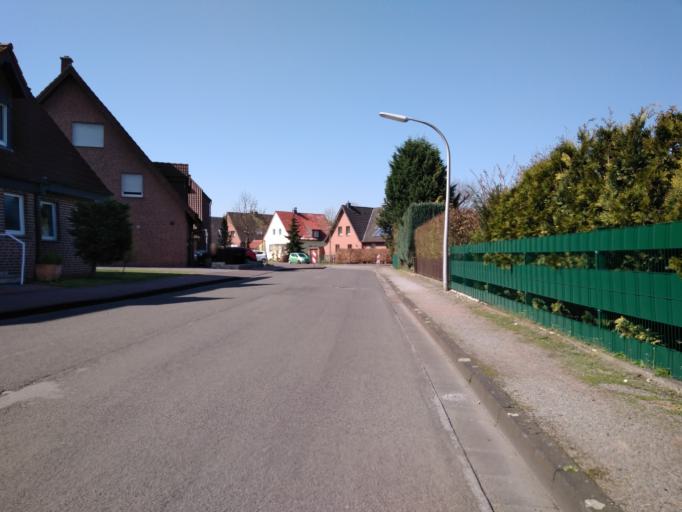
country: DE
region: North Rhine-Westphalia
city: Dorsten
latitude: 51.6644
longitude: 6.9487
